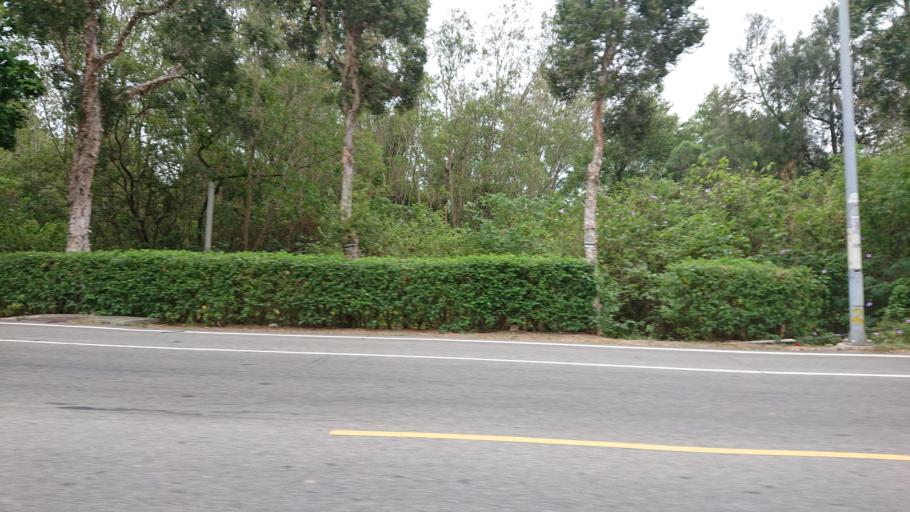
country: TW
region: Fukien
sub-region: Kinmen
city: Jincheng
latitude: 24.4392
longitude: 118.3985
